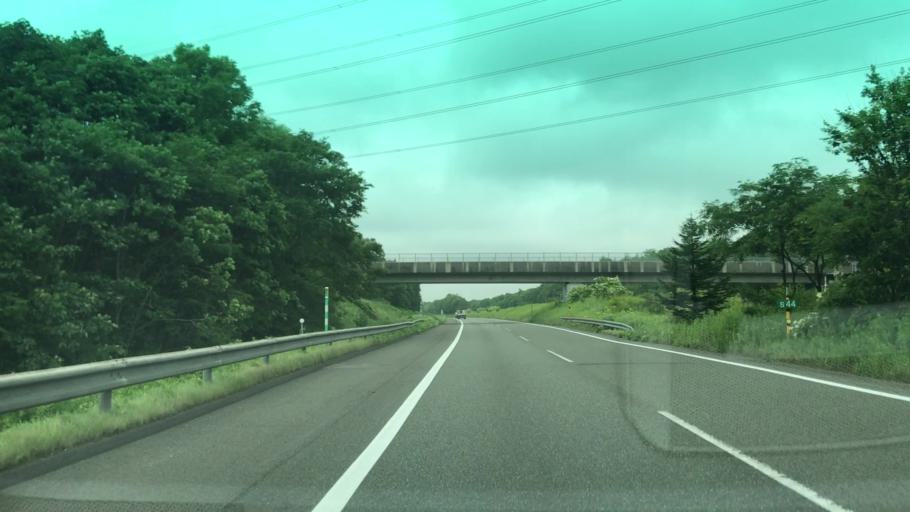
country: JP
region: Hokkaido
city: Chitose
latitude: 42.7384
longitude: 141.6517
